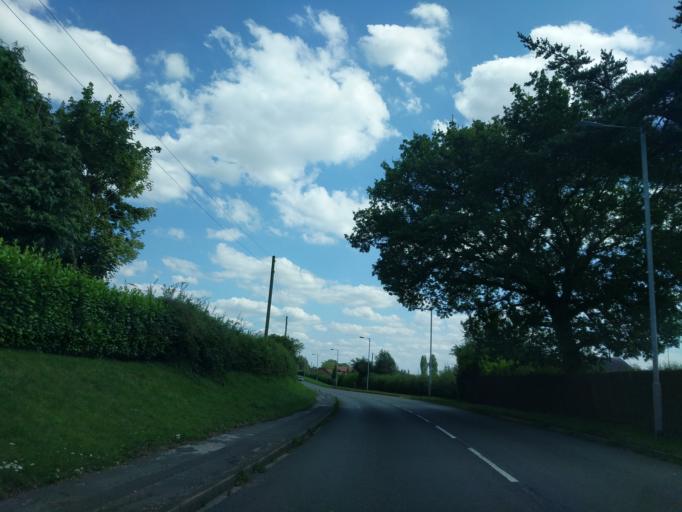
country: GB
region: England
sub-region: Staffordshire
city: Cheadle
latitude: 52.9418
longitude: -1.9669
